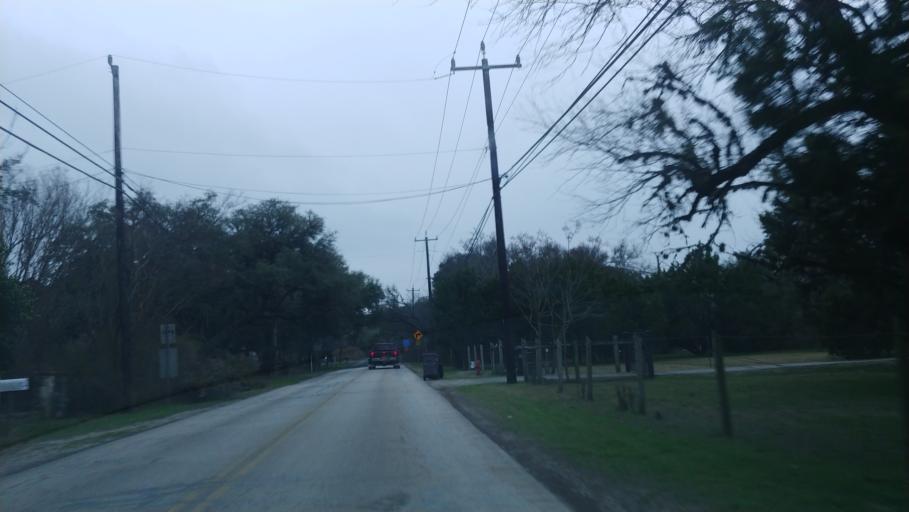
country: US
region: Texas
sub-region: Bexar County
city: Helotes
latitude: 29.6101
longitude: -98.6847
